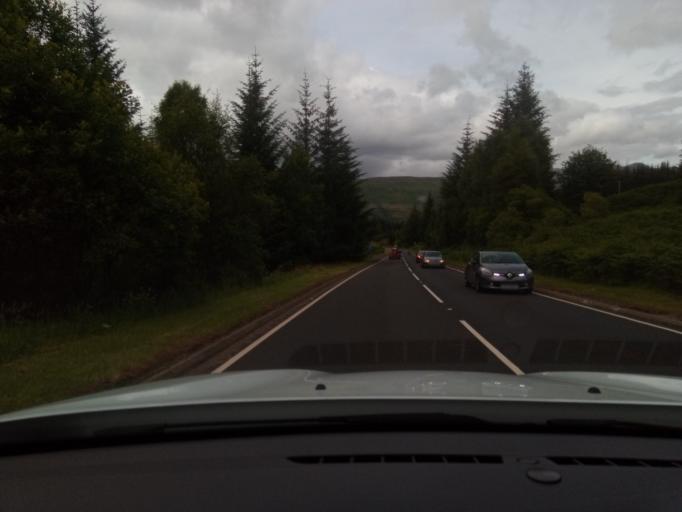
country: GB
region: Scotland
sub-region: Stirling
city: Callander
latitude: 56.4318
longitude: -4.3412
